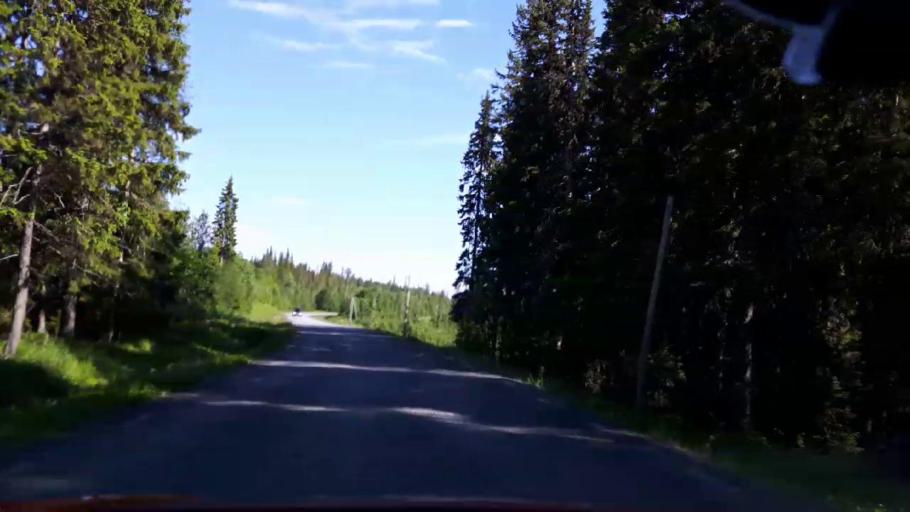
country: SE
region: Jaemtland
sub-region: Krokoms Kommun
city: Valla
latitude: 63.7110
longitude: 14.1380
